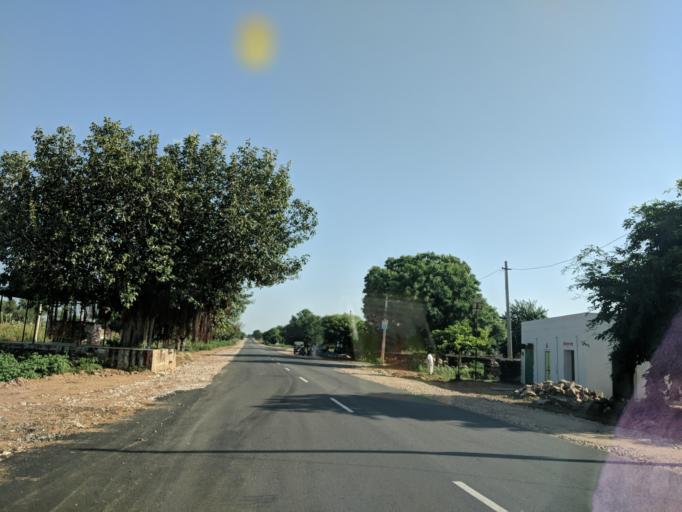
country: IN
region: Rajasthan
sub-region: Sikar
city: Losal
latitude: 27.3910
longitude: 75.0670
